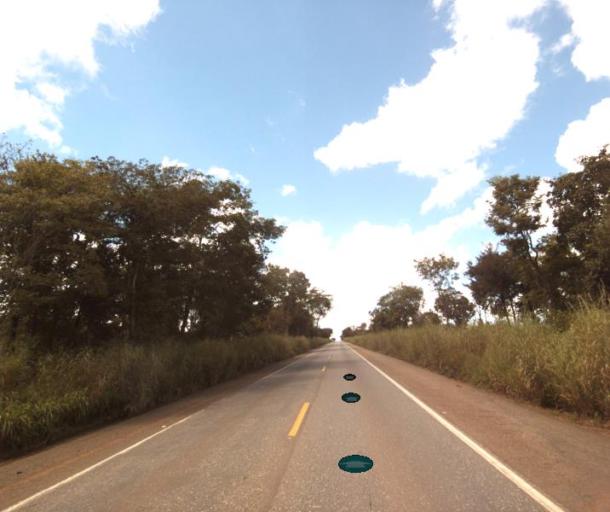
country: BR
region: Goias
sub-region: Petrolina De Goias
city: Petrolina de Goias
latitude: -15.9425
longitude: -49.1948
